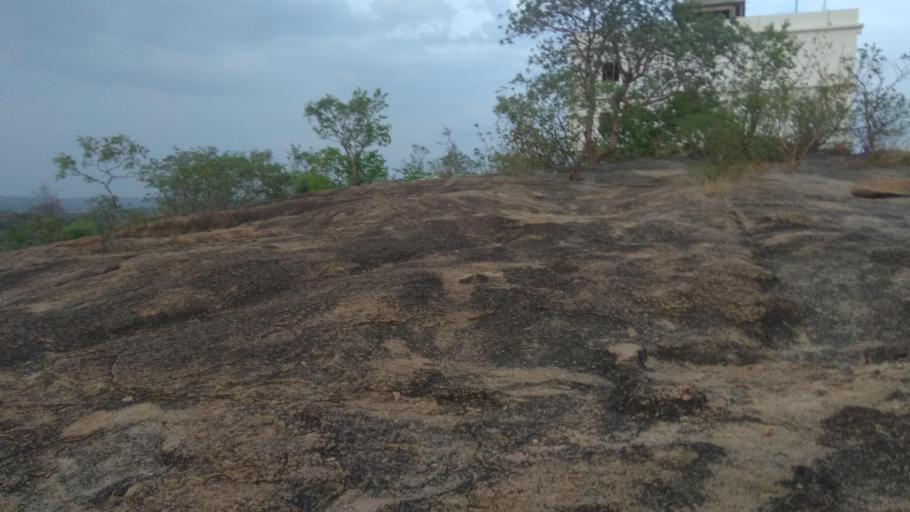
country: IN
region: Telangana
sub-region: Mahbubnagar
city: Farrukhnagar
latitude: 16.8894
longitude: 78.5051
